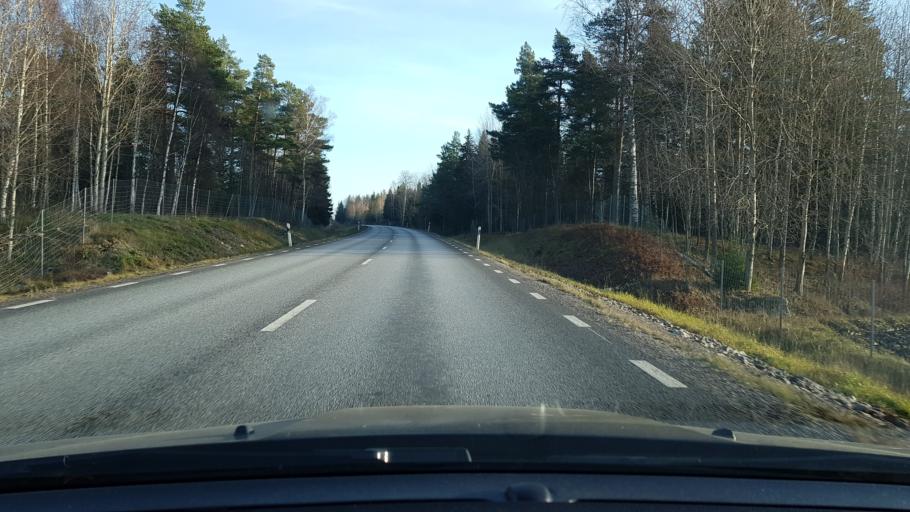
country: SE
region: Stockholm
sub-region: Vallentuna Kommun
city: Vallentuna
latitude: 59.7466
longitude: 18.0824
